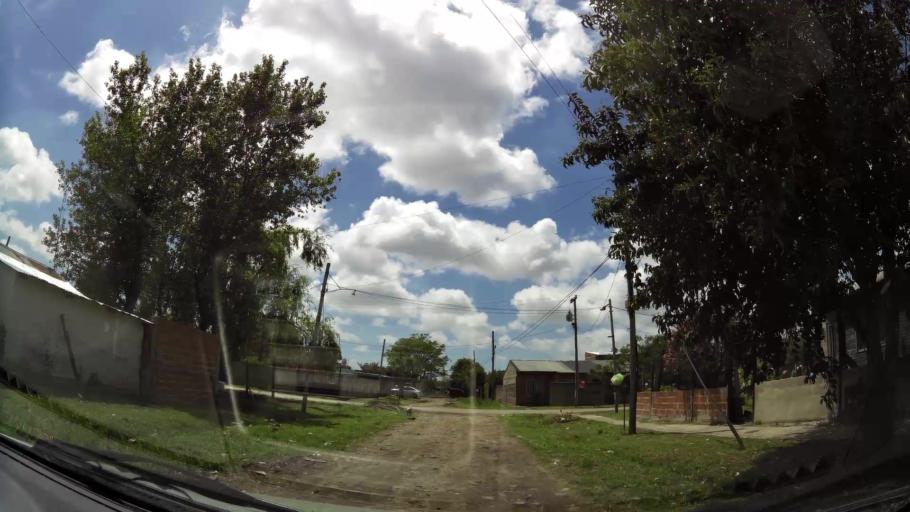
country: AR
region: Buenos Aires
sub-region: Partido de Quilmes
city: Quilmes
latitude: -34.8296
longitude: -58.2414
